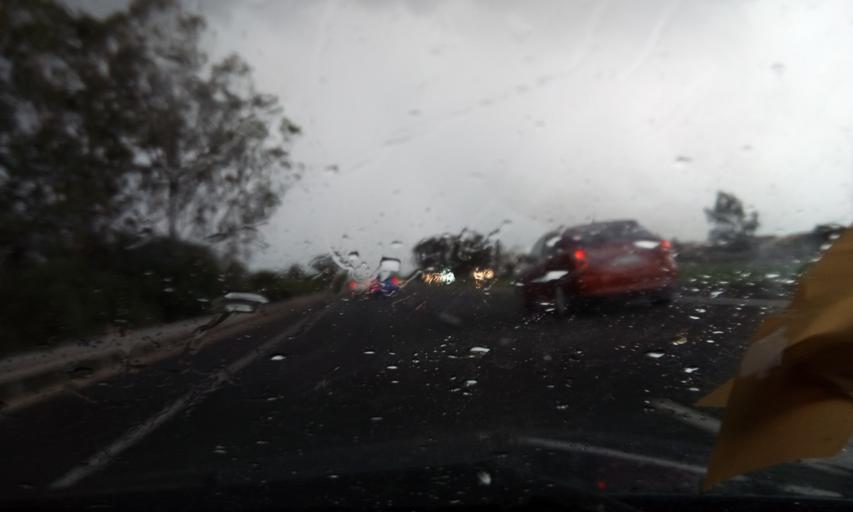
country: AU
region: New South Wales
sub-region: Camden
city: Narellan Vale
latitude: -34.0547
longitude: 150.7361
